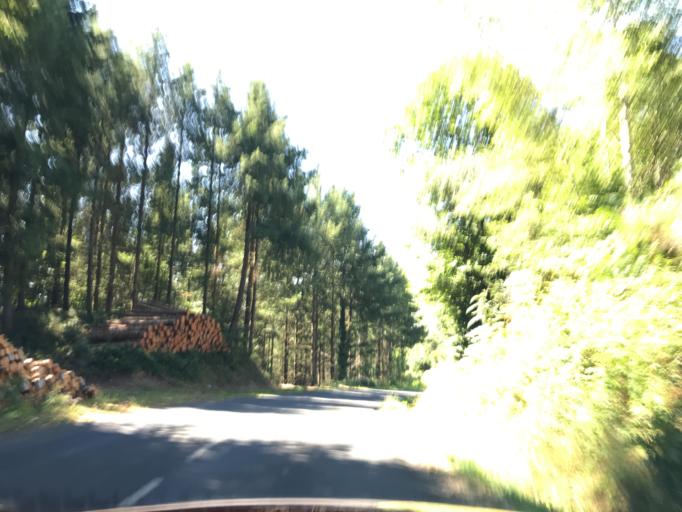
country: FR
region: Auvergne
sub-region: Departement du Puy-de-Dome
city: Courpiere
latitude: 45.7443
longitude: 3.6494
